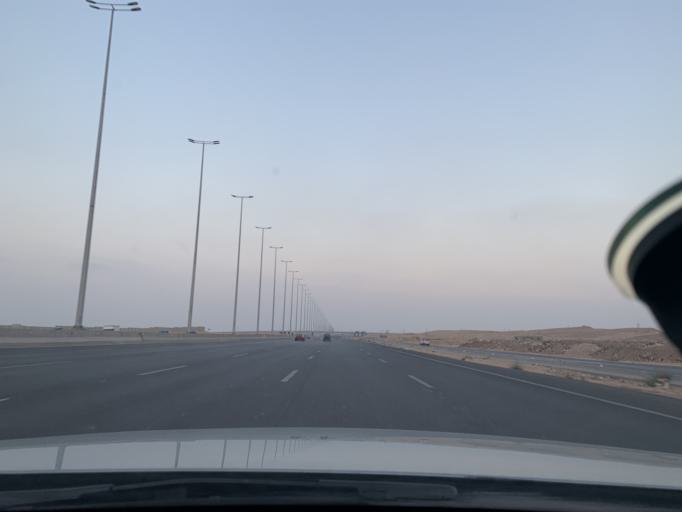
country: EG
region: Muhafazat al Qalyubiyah
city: Al Khankah
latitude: 30.0931
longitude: 31.4943
